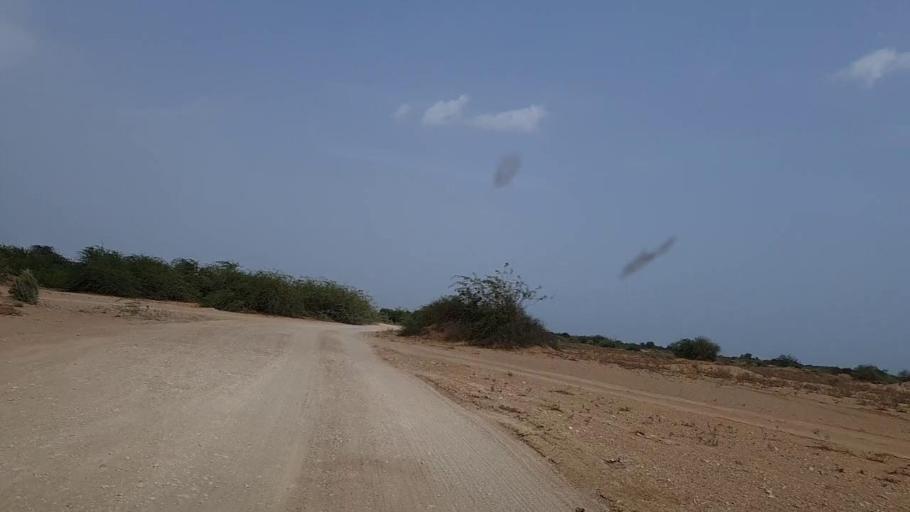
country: PK
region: Sindh
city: Kotri
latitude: 25.2782
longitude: 68.2490
